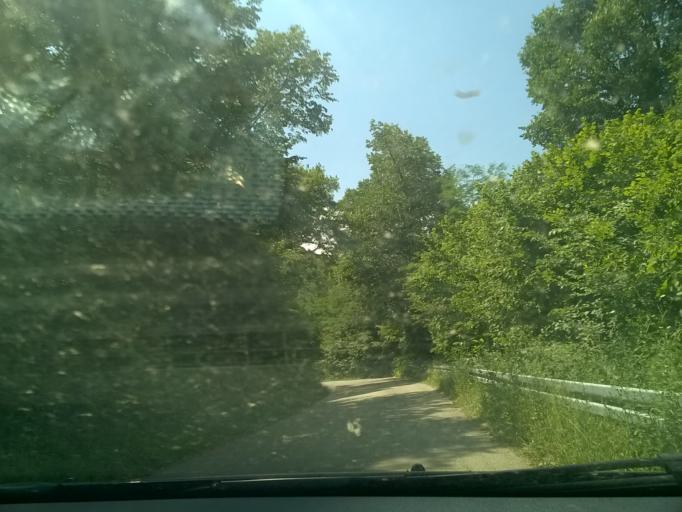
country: RS
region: Central Serbia
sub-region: Zajecarski Okrug
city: Soko Banja
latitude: 43.6376
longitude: 21.8729
